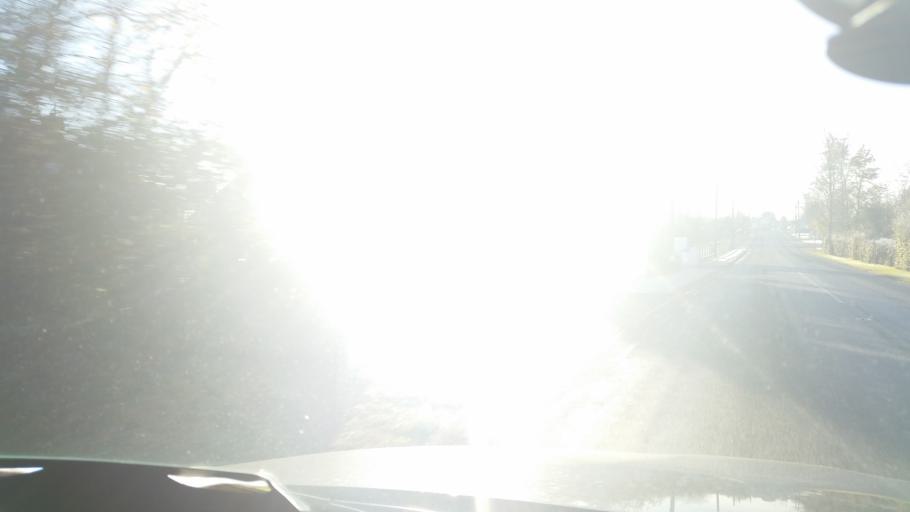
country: IE
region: Leinster
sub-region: Loch Garman
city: Gorey
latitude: 52.6136
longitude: -6.3062
